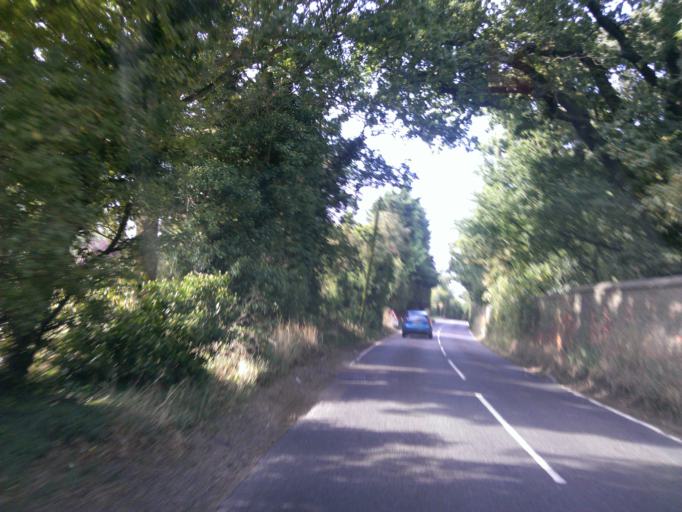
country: GB
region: England
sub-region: Essex
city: Great Totham
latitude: 51.8064
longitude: 0.6801
